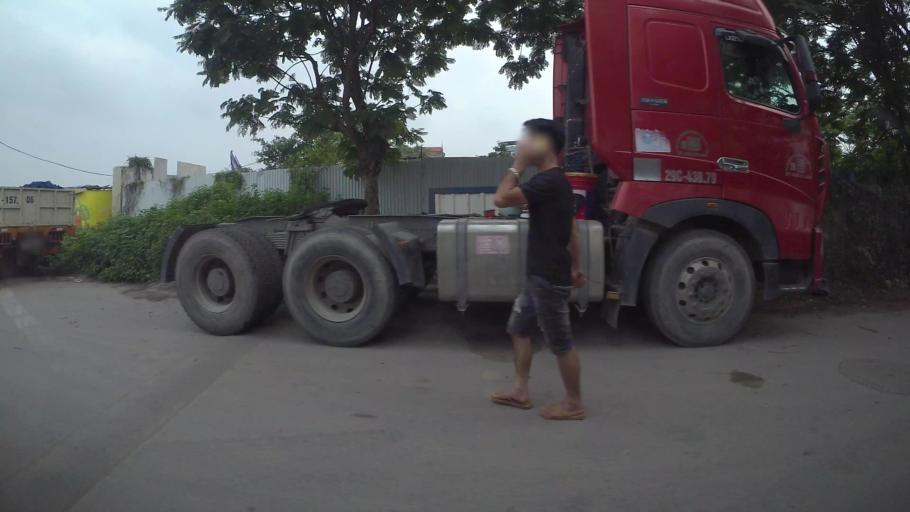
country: VN
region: Ha Noi
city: Trau Quy
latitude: 21.0659
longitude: 105.8998
